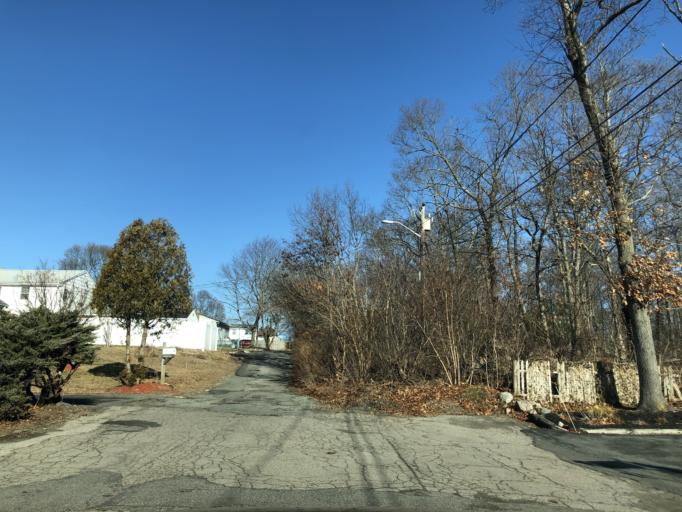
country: US
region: Massachusetts
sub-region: Plymouth County
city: Brockton
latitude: 42.1002
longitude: -71.0024
